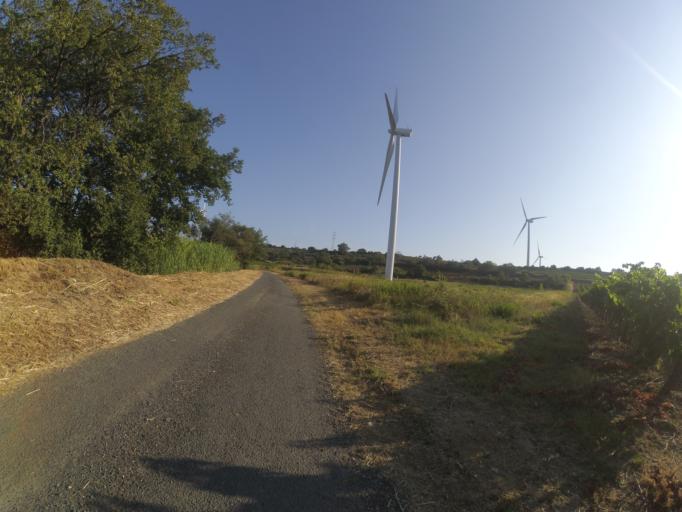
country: FR
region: Languedoc-Roussillon
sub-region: Departement des Pyrenees-Orientales
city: Pezilla-la-Riviere
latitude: 42.7149
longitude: 2.7693
